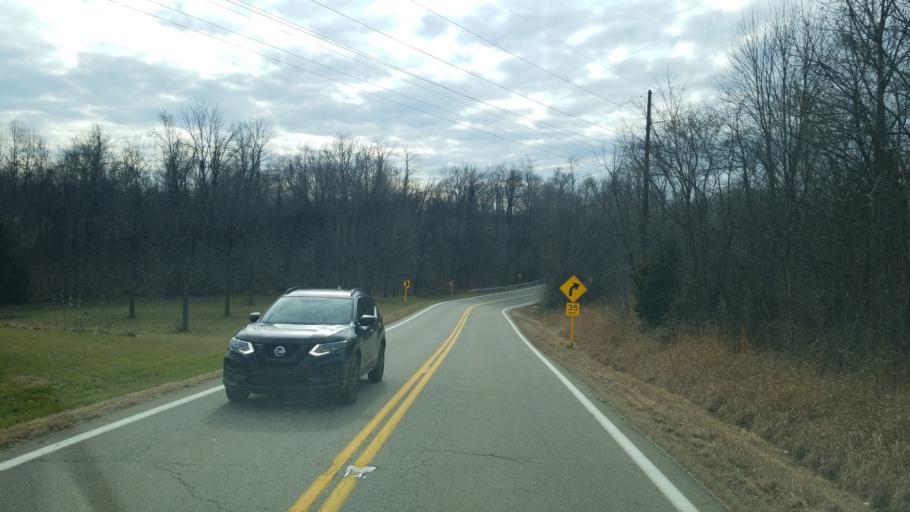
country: US
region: Ohio
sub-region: Ross County
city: Frankfort
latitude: 39.3517
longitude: -83.1673
